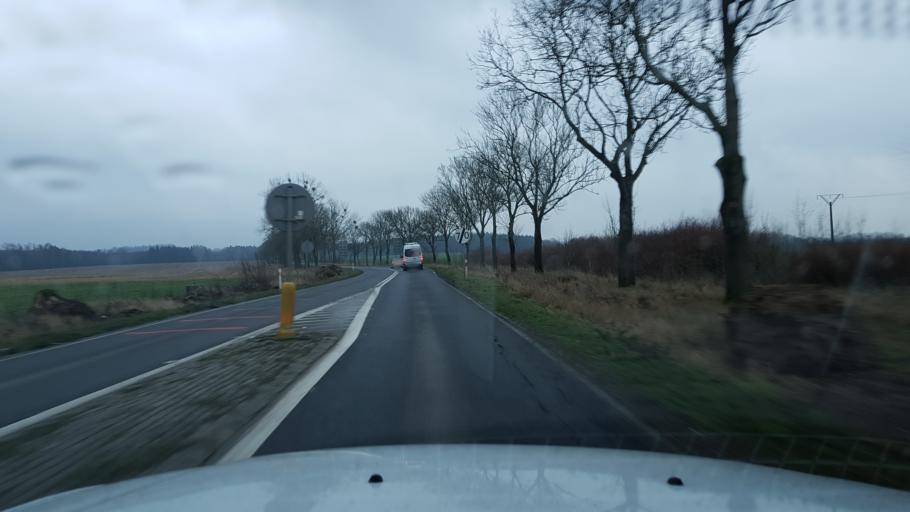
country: PL
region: West Pomeranian Voivodeship
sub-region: Powiat gryficki
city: Gryfice
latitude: 53.8689
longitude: 15.2168
